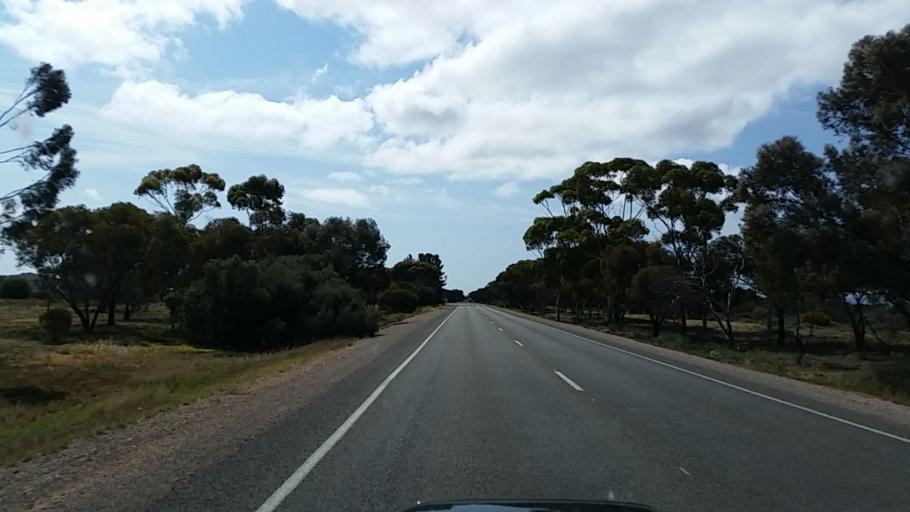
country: AU
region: South Australia
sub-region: Port Pirie City and Dists
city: Solomontown
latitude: -33.2286
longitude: 138.0134
